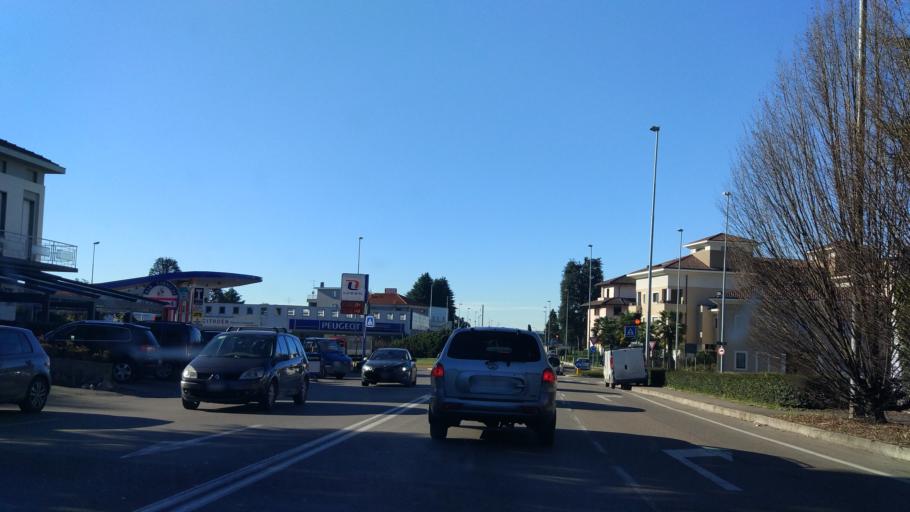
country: IT
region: Lombardy
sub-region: Provincia di Monza e Brianza
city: Giussano
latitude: 45.6973
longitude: 9.2152
